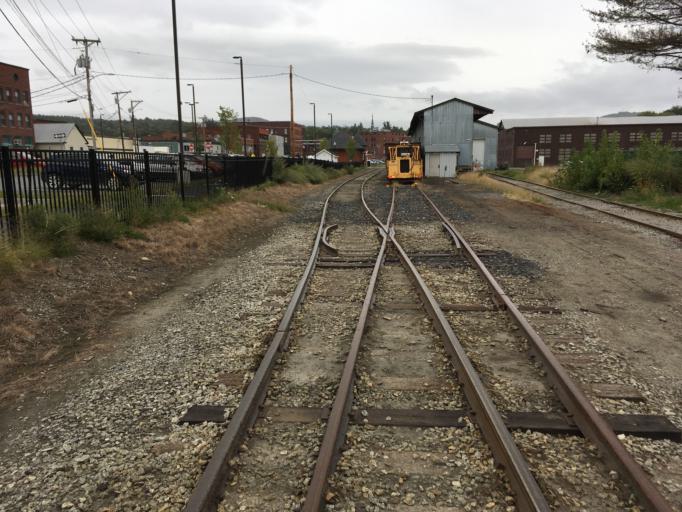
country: US
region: Vermont
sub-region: Washington County
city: Barre
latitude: 44.1996
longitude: -72.5058
